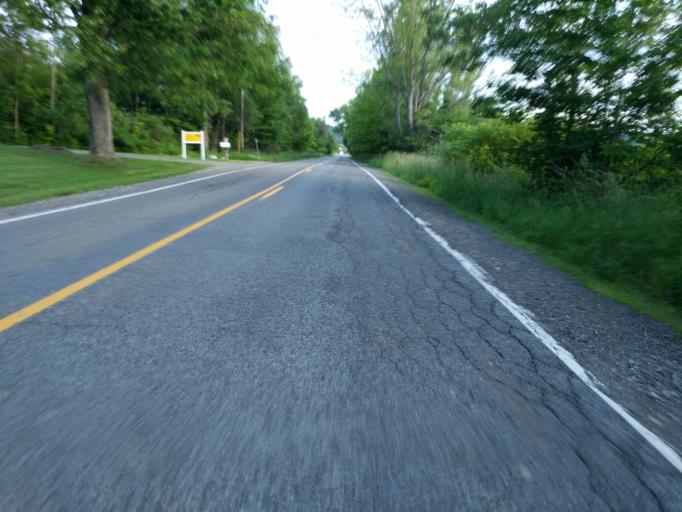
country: US
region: New York
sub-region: Tompkins County
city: Dryden
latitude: 42.4069
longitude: -76.3507
